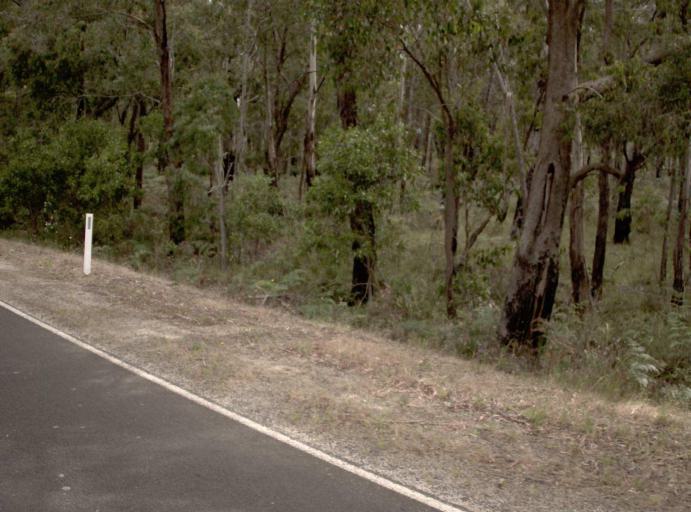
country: AU
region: Victoria
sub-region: Latrobe
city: Traralgon
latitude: -38.4199
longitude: 146.8166
